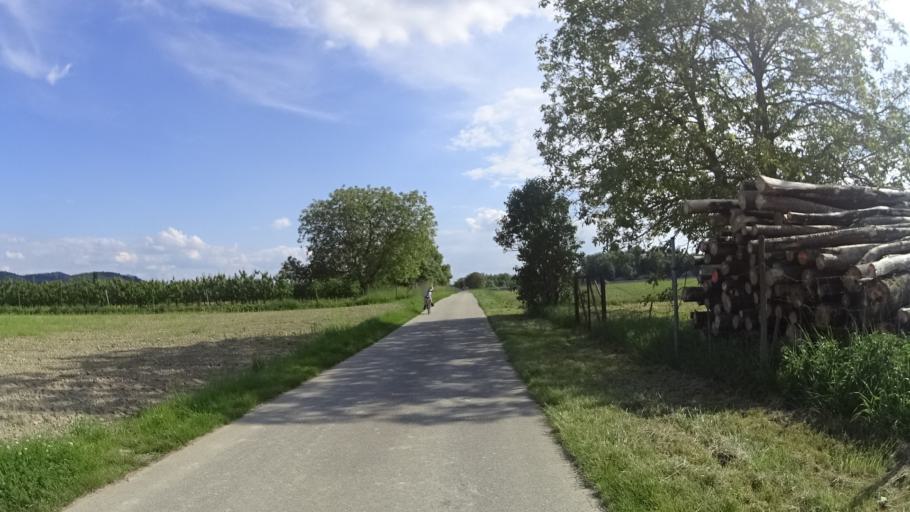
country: DE
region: Baden-Wuerttemberg
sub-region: Freiburg Region
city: Vogtsburg
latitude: 48.0871
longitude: 7.5936
